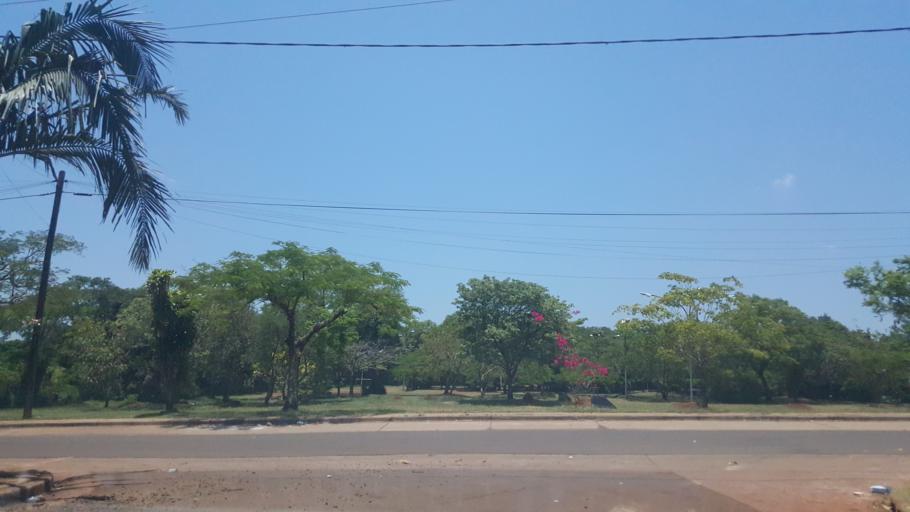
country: AR
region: Misiones
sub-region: Departamento de Capital
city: Posadas
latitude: -27.4060
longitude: -55.8965
